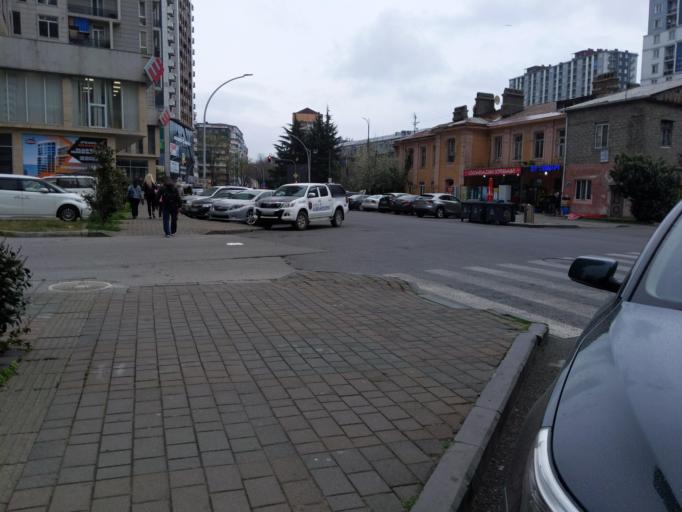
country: GE
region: Ajaria
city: Batumi
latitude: 41.6423
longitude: 41.6180
